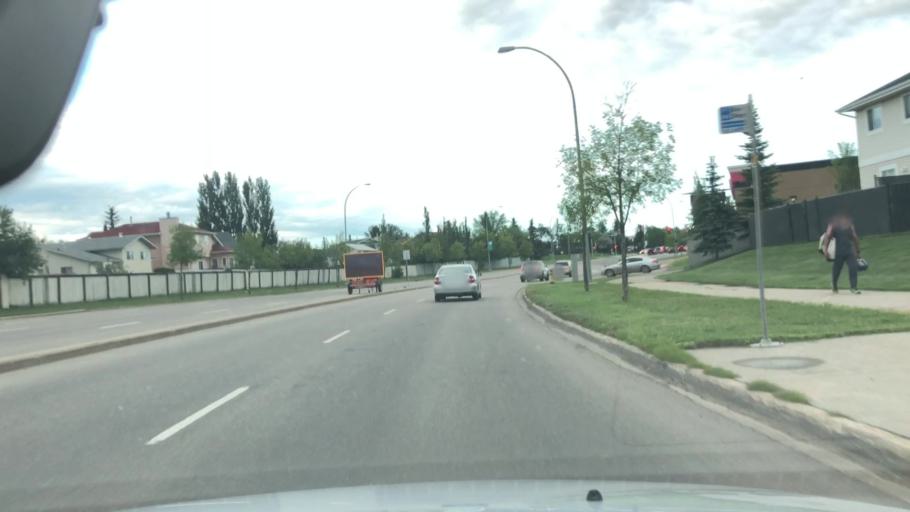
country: CA
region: Alberta
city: St. Albert
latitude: 53.6167
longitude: -113.5449
